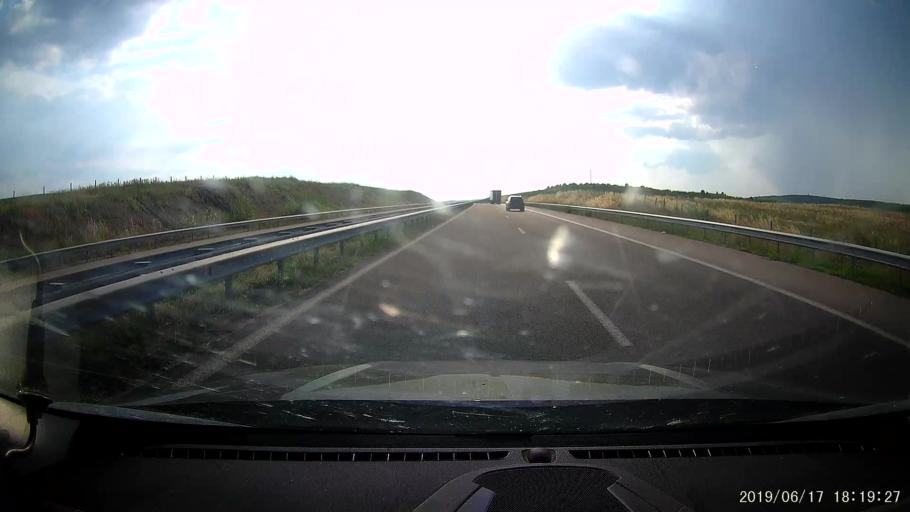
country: BG
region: Khaskovo
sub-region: Obshtina Kharmanli
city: Kharmanli
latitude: 41.9624
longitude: 25.8460
